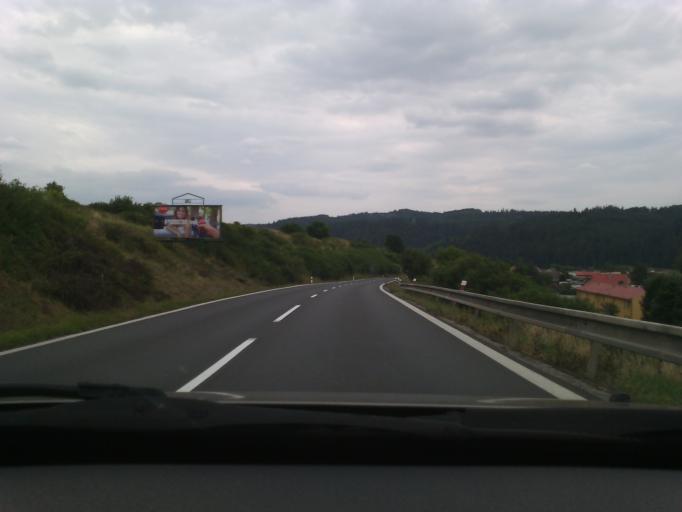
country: SK
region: Presovsky
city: Spisska Bela
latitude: 49.1774
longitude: 20.4536
